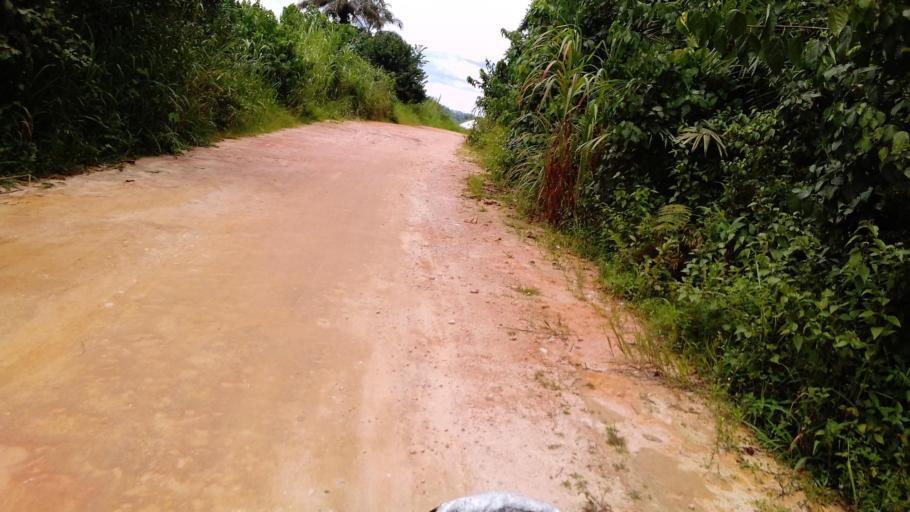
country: SL
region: Eastern Province
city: Koyima
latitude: 8.6924
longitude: -11.0100
